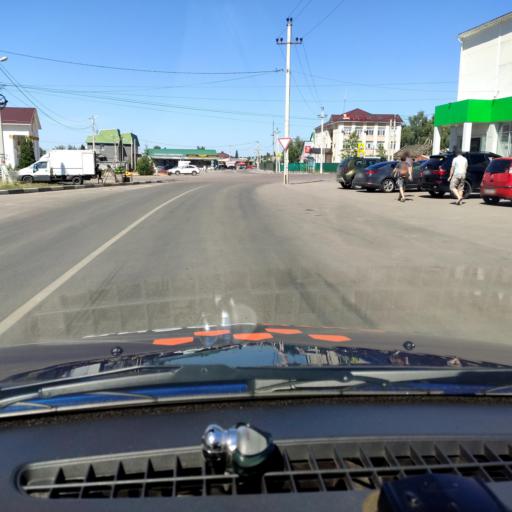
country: RU
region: Voronezj
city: Podgornoye
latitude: 51.7896
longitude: 39.1457
